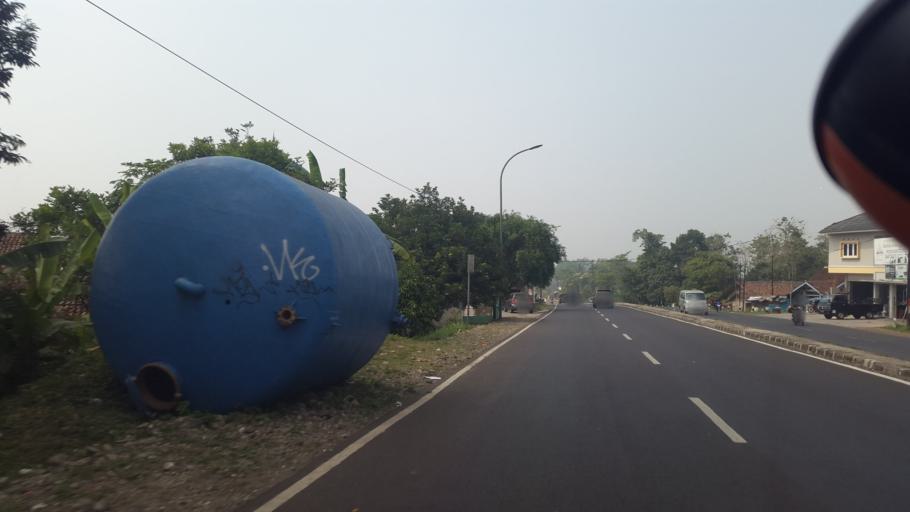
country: ID
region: West Java
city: Sukabumi
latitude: -6.9360
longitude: 106.9059
